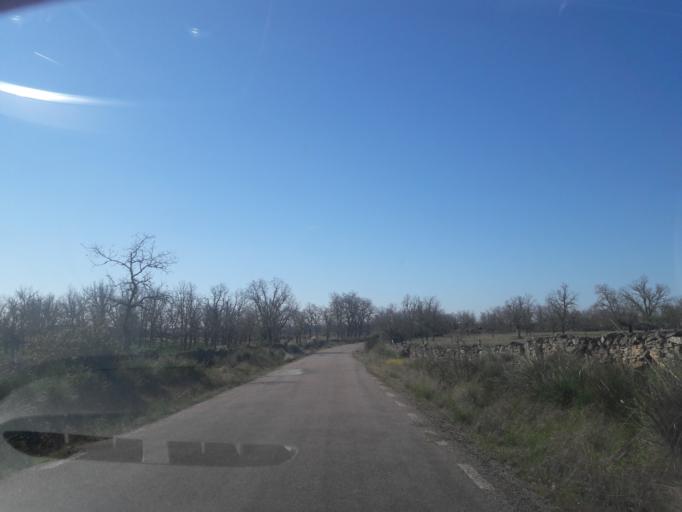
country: ES
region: Castille and Leon
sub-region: Provincia de Salamanca
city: Valsalabroso
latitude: 41.1162
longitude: -6.4832
